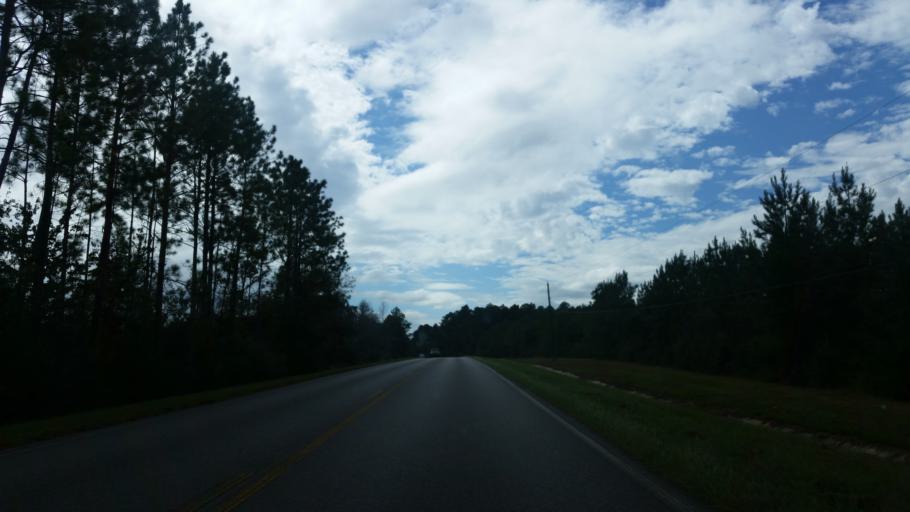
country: US
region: Florida
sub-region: Santa Rosa County
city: Point Baker
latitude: 30.7052
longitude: -86.9758
